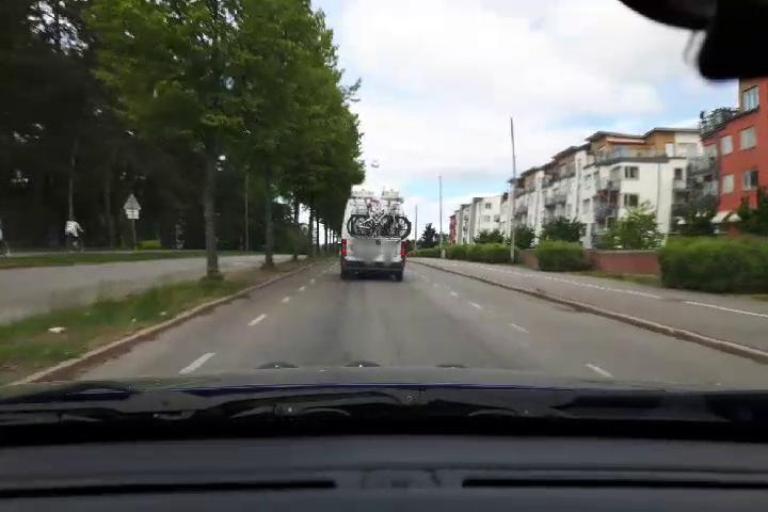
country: SE
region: Uppsala
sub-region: Uppsala Kommun
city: Gamla Uppsala
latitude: 59.8774
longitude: 17.6235
